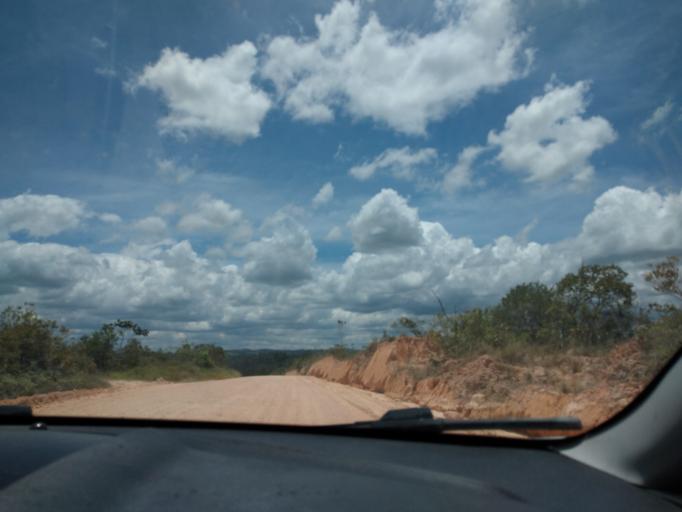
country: BR
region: Minas Gerais
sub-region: Tiradentes
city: Tiradentes
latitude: -20.9142
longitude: -44.2661
